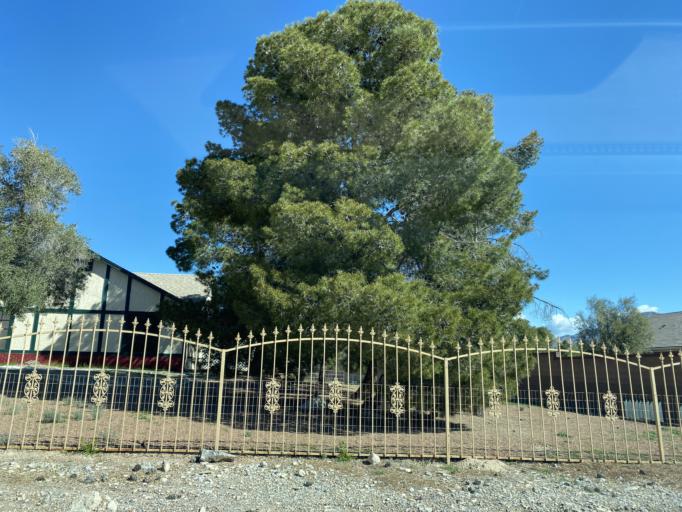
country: US
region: Nevada
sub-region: Clark County
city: North Las Vegas
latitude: 36.3301
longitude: -115.2809
